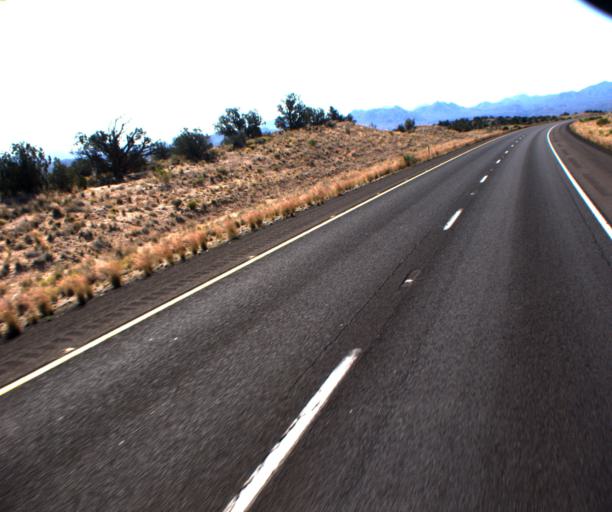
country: US
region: Arizona
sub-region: Mohave County
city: New Kingman-Butler
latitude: 35.1403
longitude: -113.6756
